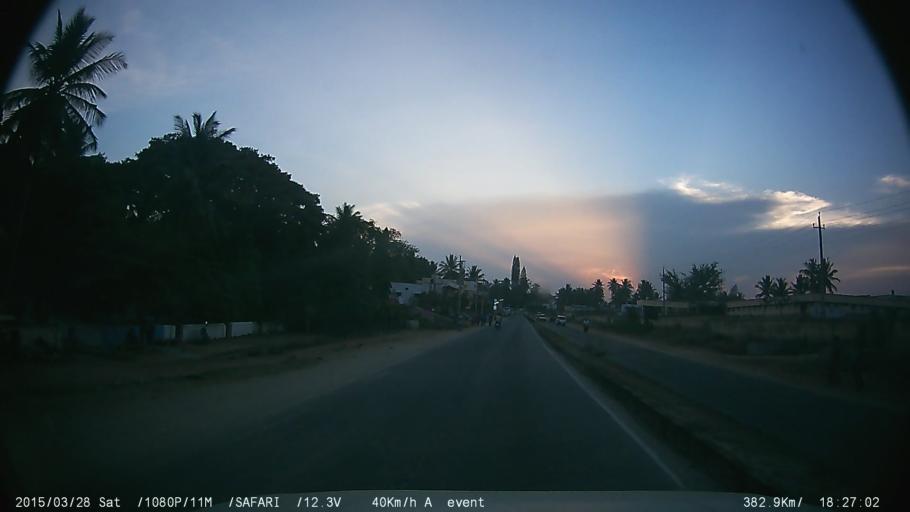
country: IN
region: Karnataka
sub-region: Mandya
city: Shrirangapattana
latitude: 12.4065
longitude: 76.5759
